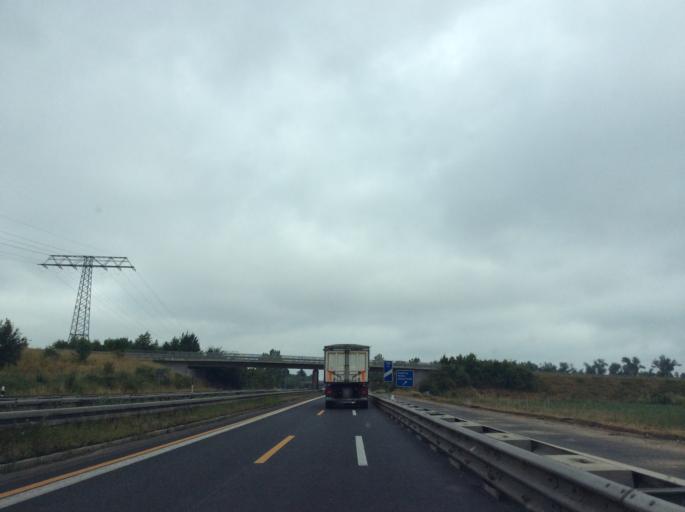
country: DE
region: Saxony
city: Radeburg
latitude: 51.2082
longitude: 13.7374
